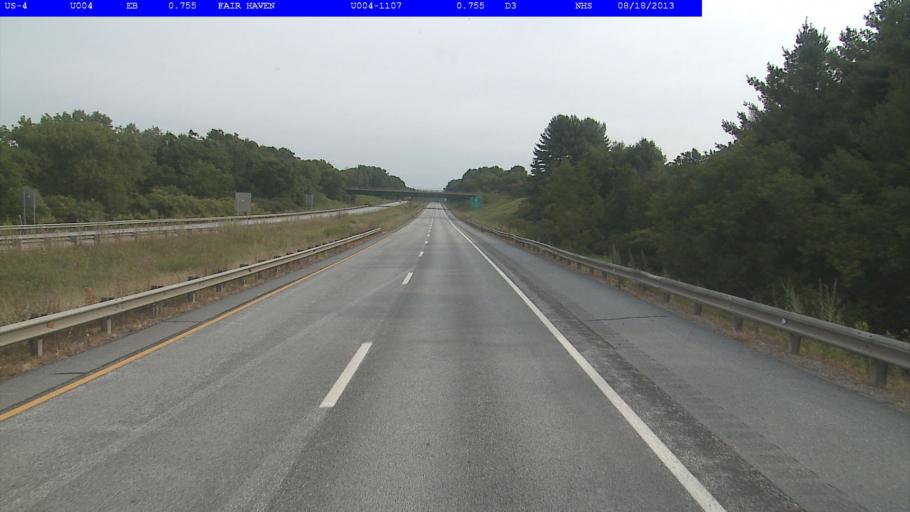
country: US
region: Vermont
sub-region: Rutland County
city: Fair Haven
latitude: 43.5936
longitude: -73.2846
